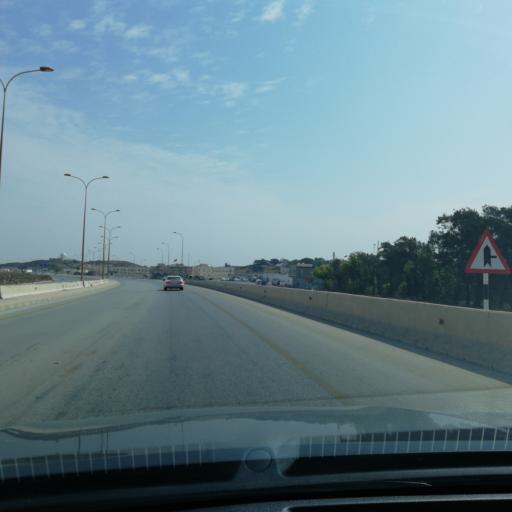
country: OM
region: Zufar
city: Salalah
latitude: 17.2488
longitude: 54.0813
